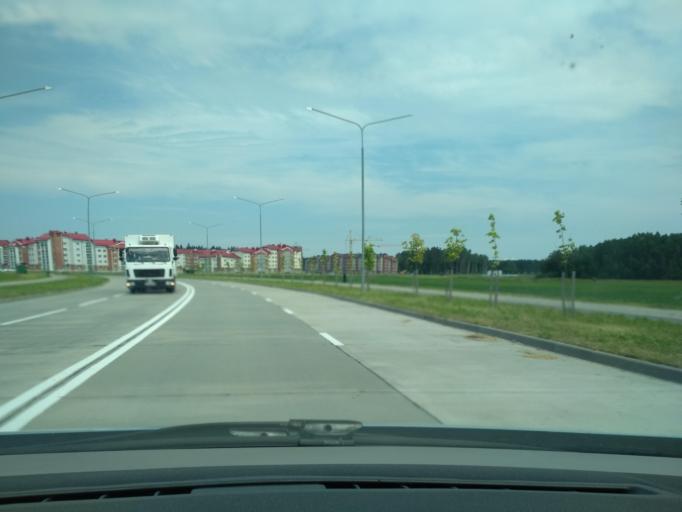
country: BY
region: Grodnenskaya
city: Astravyets
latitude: 54.5944
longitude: 25.9750
